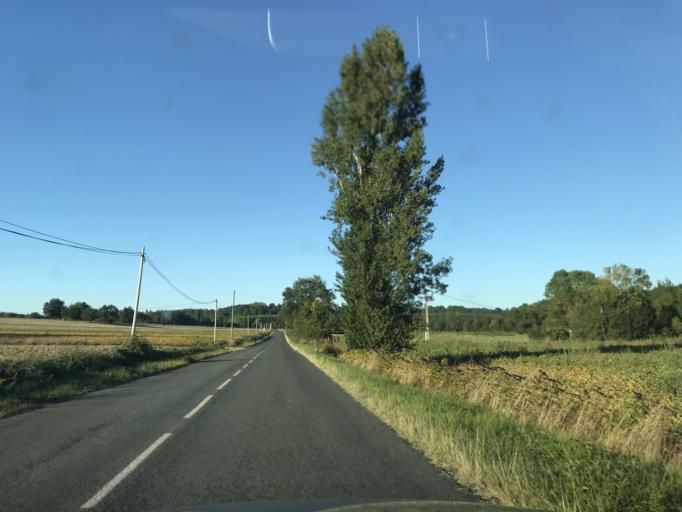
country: FR
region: Aquitaine
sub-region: Departement de la Gironde
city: Rauzan
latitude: 44.7644
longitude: -0.0660
